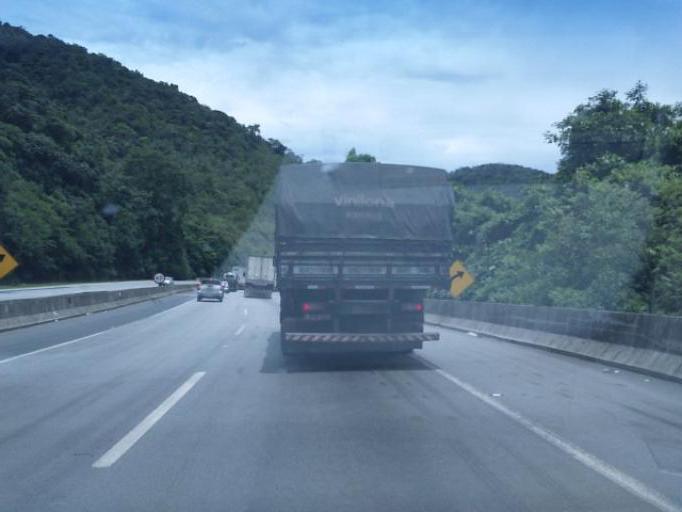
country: BR
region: Sao Paulo
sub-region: Juquitiba
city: Juquitiba
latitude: -24.0499
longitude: -47.2002
